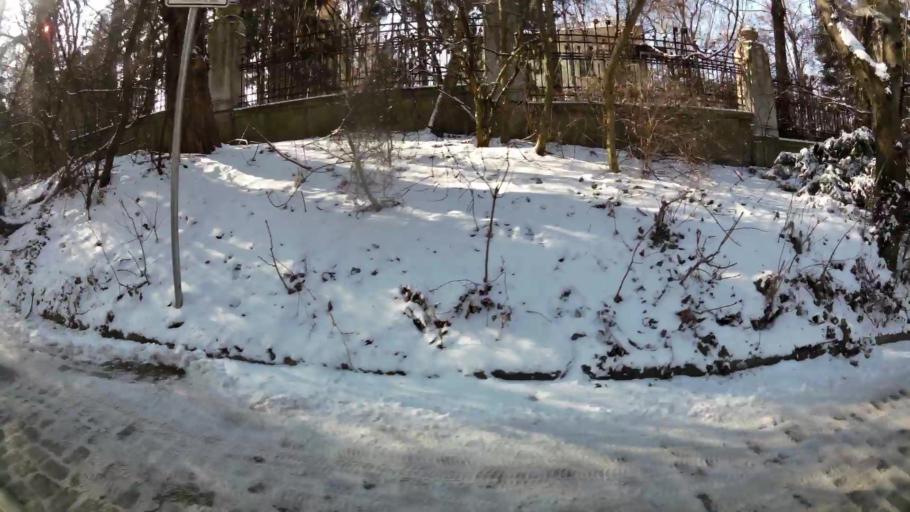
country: BG
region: Sofia-Capital
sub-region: Stolichna Obshtina
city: Sofia
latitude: 42.6757
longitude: 23.3272
